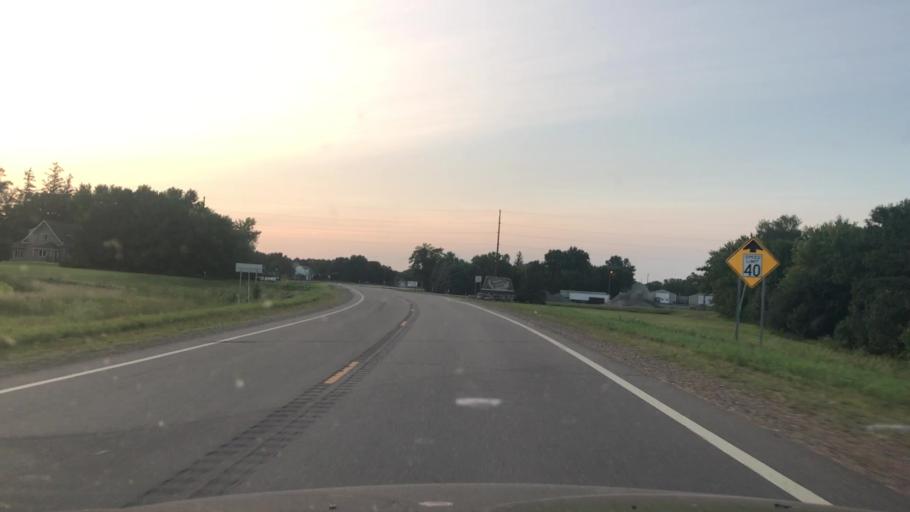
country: US
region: Minnesota
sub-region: Redwood County
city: Redwood Falls
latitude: 44.5235
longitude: -95.1181
